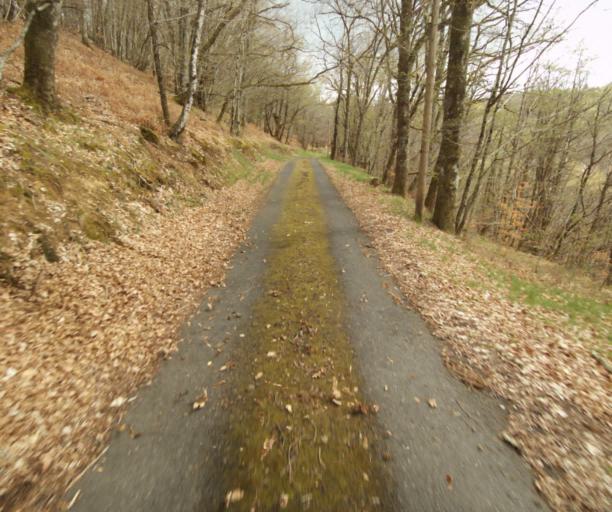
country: FR
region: Limousin
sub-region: Departement de la Correze
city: Naves
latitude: 45.3167
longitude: 1.8117
